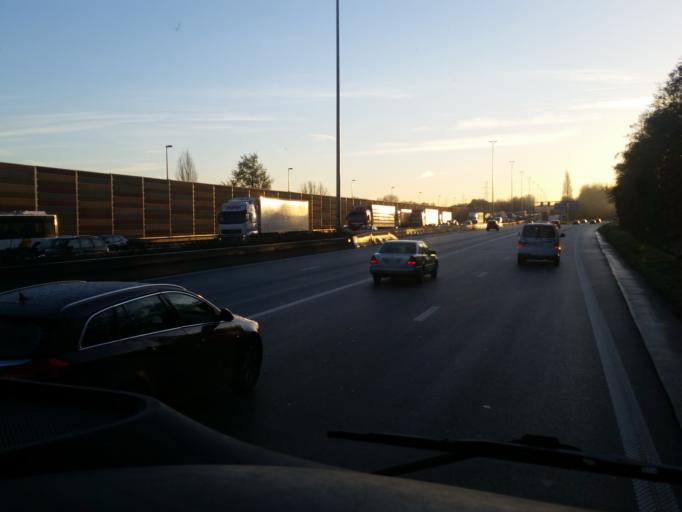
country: BE
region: Flanders
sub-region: Provincie Antwerpen
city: Ranst
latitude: 51.2026
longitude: 4.5716
